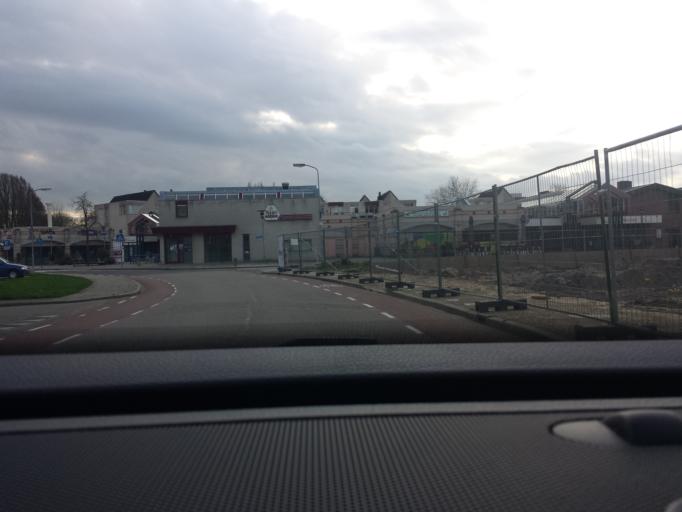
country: NL
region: Gelderland
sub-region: Gemeente Duiven
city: Duiven
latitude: 51.9489
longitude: 6.0239
